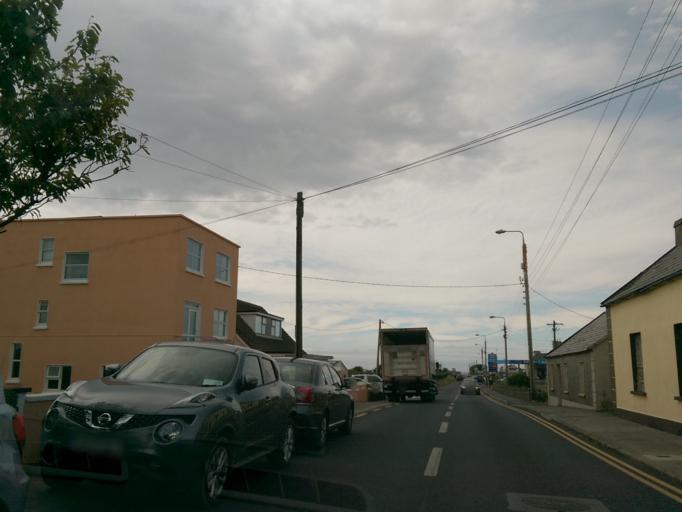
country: IE
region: Munster
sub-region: An Clar
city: Kilrush
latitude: 52.8574
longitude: -9.4023
